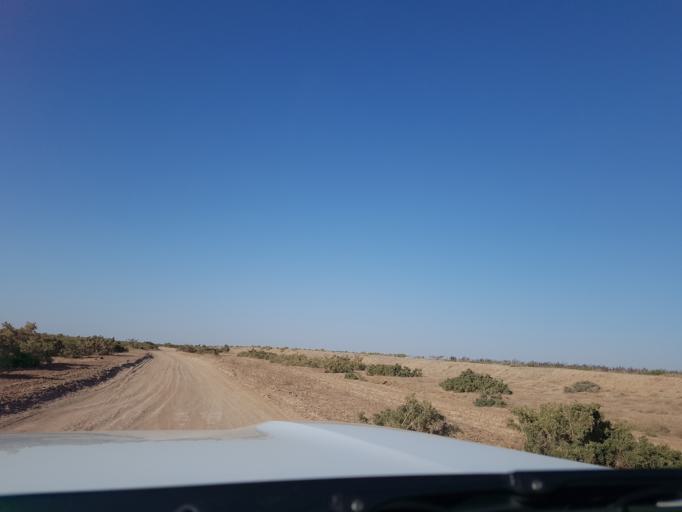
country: IR
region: Razavi Khorasan
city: Sarakhs
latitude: 36.9852
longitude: 61.3868
